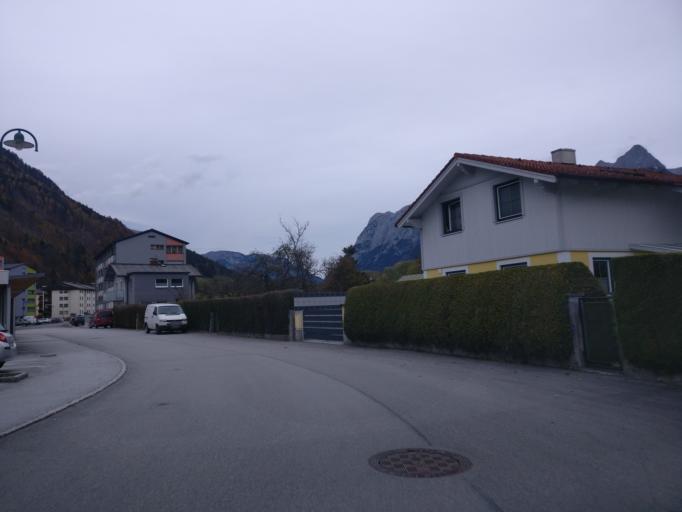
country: AT
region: Salzburg
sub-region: Politischer Bezirk Sankt Johann im Pongau
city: Bischofshofen
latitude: 47.4274
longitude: 13.2170
